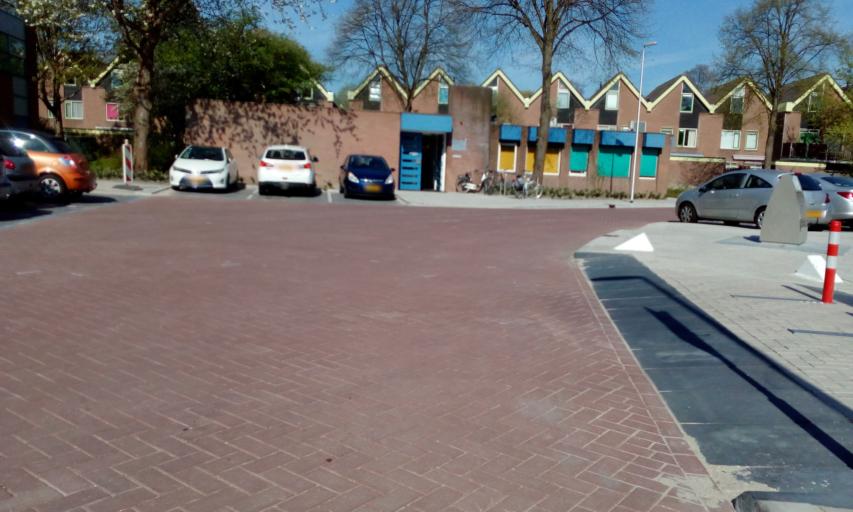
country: NL
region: South Holland
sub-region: Gemeente Zoetermeer
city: Zoetermeer
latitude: 52.0652
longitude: 4.4854
